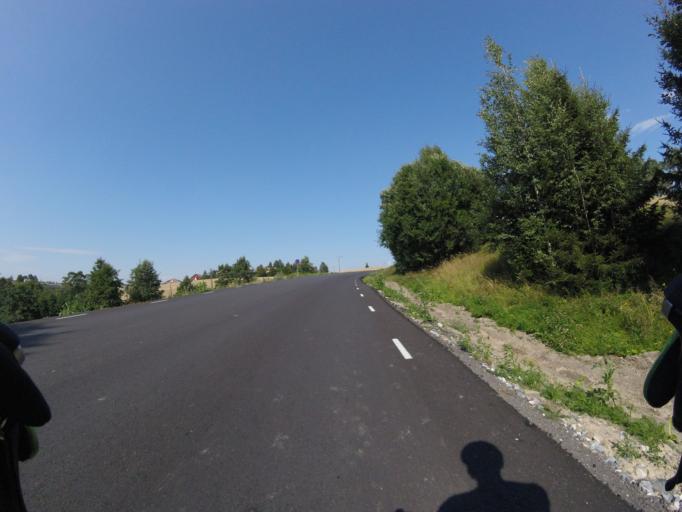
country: NO
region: Akershus
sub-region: Ullensaker
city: Klofta
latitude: 60.0828
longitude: 11.1626
